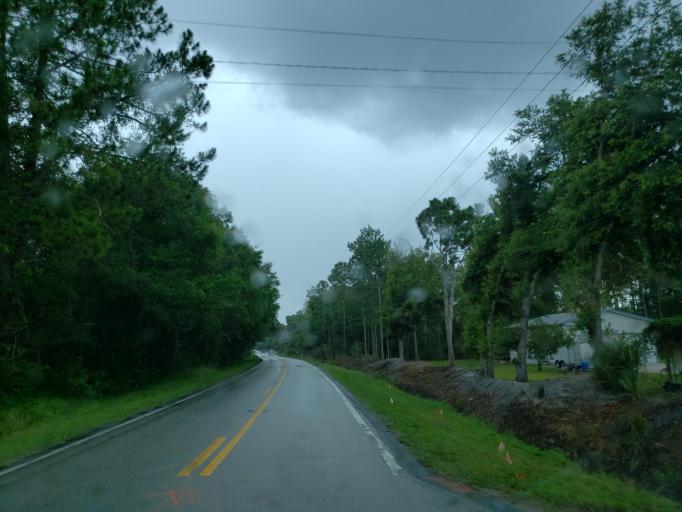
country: US
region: Florida
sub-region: Pasco County
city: Wesley Chapel
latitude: 28.2627
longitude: -82.3692
